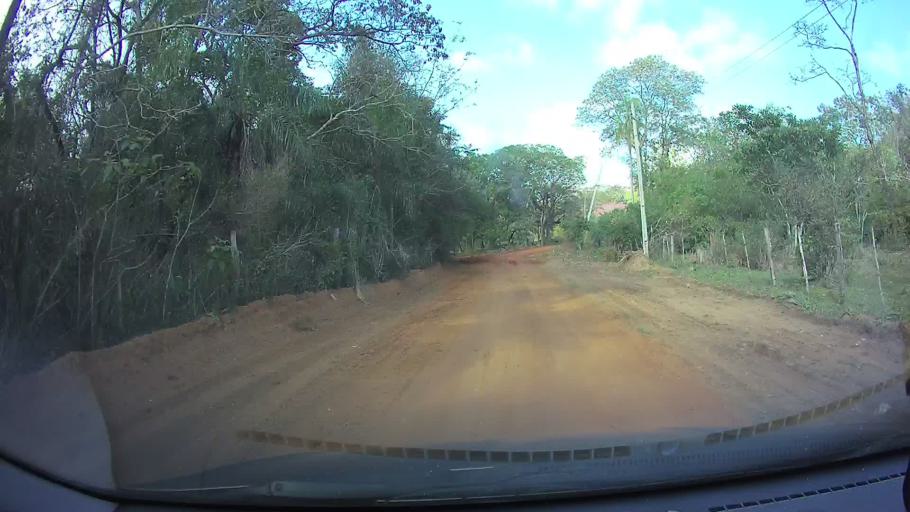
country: PY
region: Cordillera
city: Arroyos y Esteros
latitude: -25.0230
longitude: -57.1889
